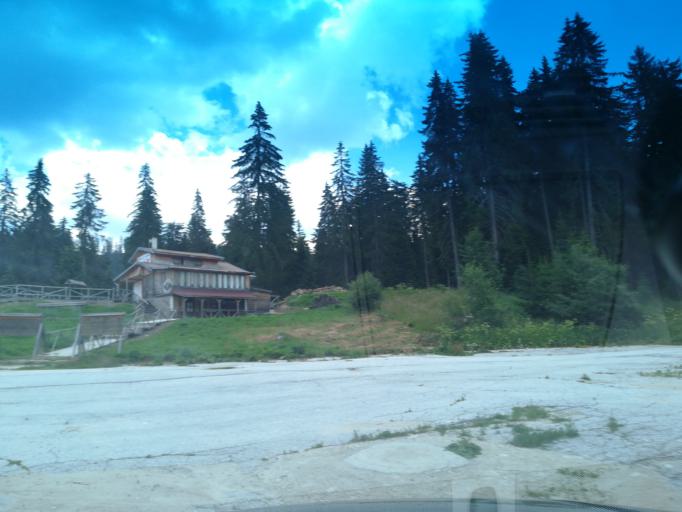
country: BG
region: Smolyan
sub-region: Obshtina Smolyan
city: Smolyan
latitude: 41.6553
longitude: 24.6815
